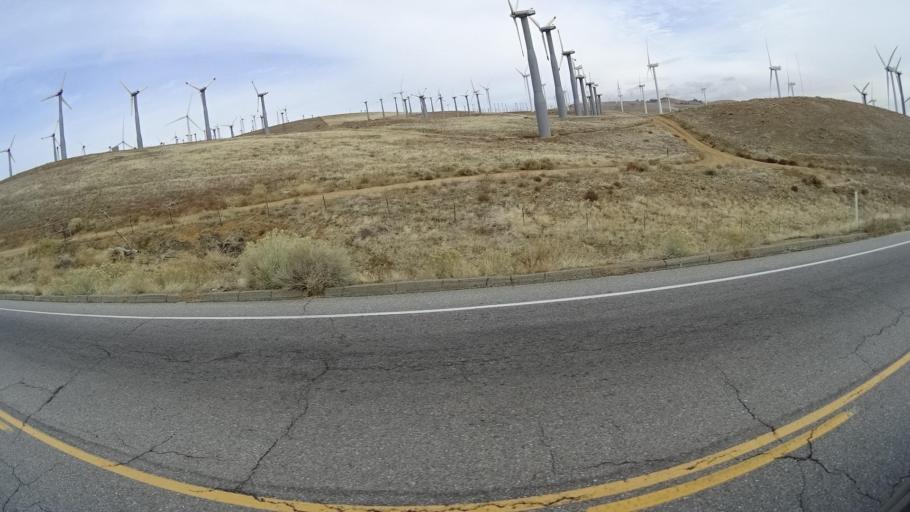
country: US
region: California
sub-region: Kern County
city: Tehachapi
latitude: 35.0576
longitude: -118.3837
